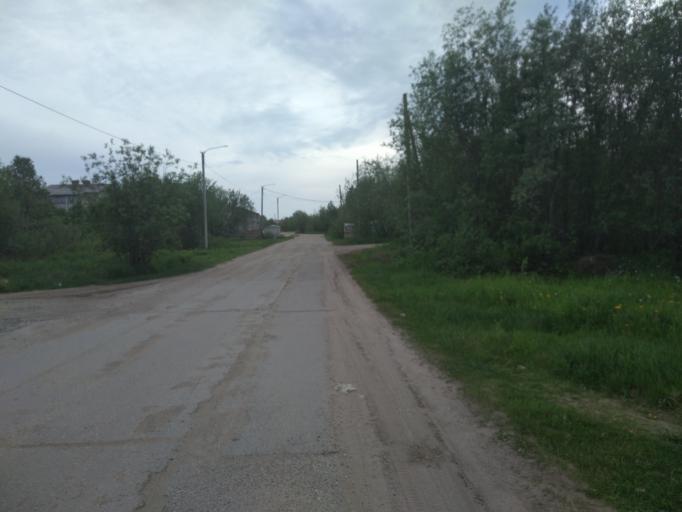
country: RU
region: Komi Republic
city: Pechora
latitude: 65.1422
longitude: 57.2465
